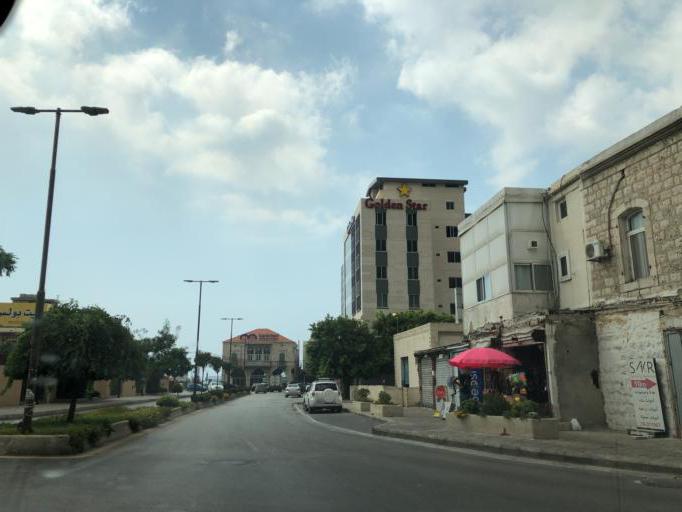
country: LB
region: Mont-Liban
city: Djounie
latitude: 33.9878
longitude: 35.6388
